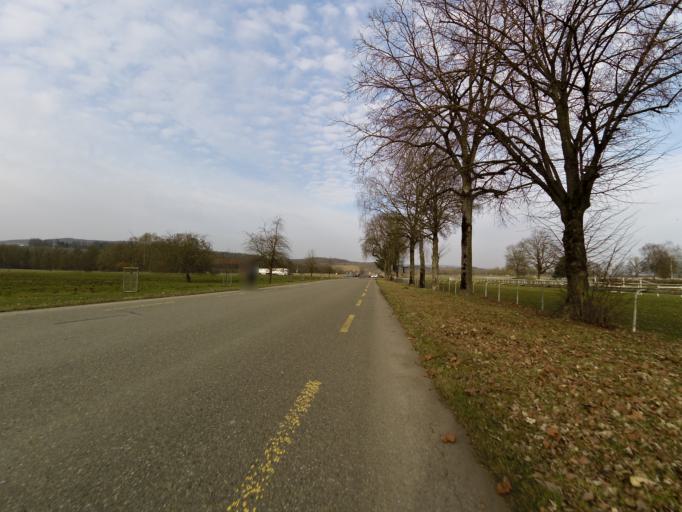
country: CH
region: Thurgau
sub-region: Frauenfeld District
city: Frauenfeld
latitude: 47.5737
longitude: 8.9020
